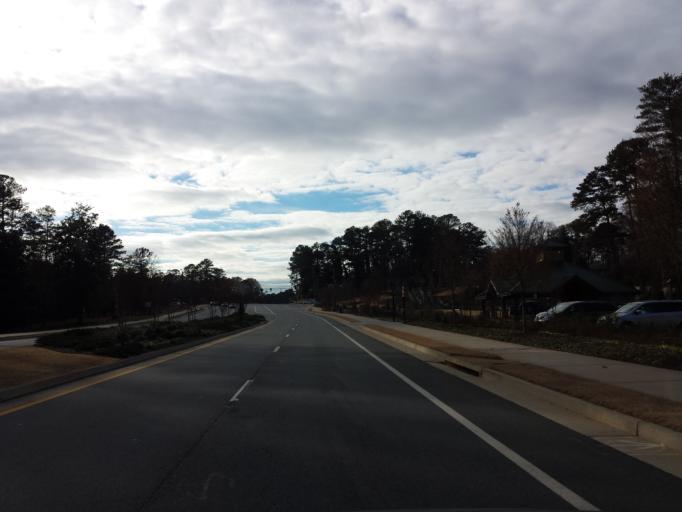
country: US
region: Georgia
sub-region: Fulton County
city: Sandy Springs
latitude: 33.9362
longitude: -84.3868
